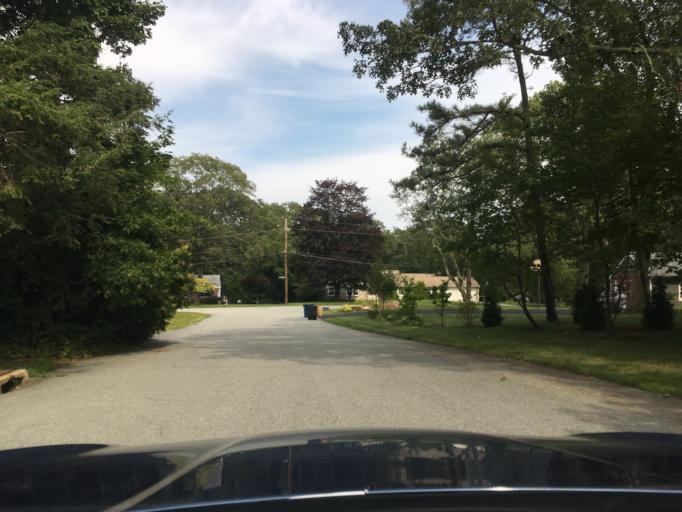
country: US
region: Rhode Island
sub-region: Kent County
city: East Greenwich
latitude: 41.6492
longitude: -71.4846
